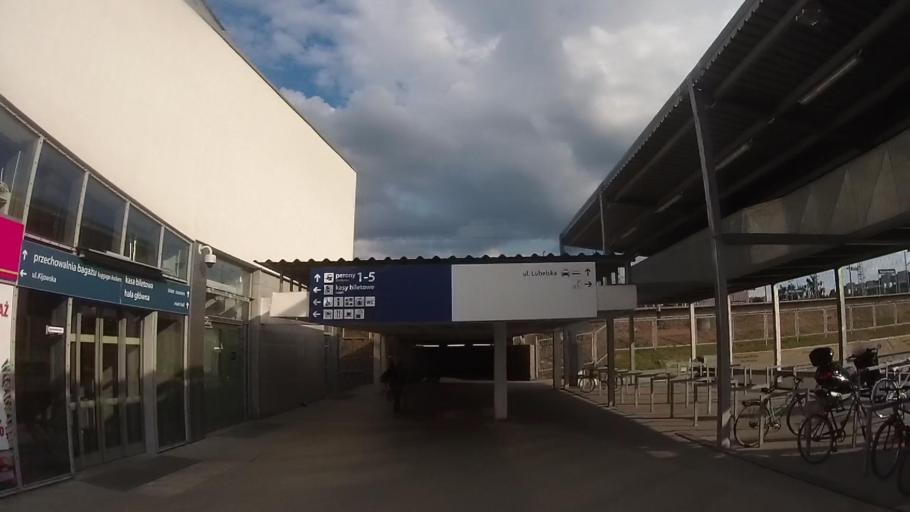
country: PL
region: Masovian Voivodeship
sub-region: Warszawa
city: Praga Polnoc
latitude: 52.2521
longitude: 21.0501
